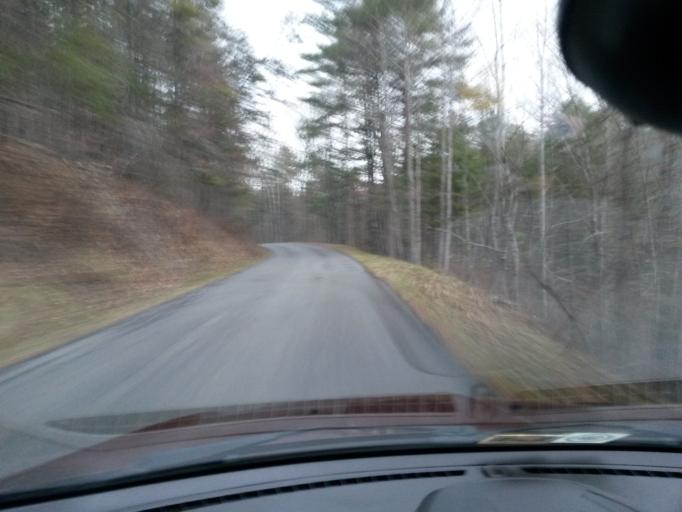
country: US
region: Virginia
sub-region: Bath County
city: Warm Springs
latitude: 37.9592
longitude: -79.7568
